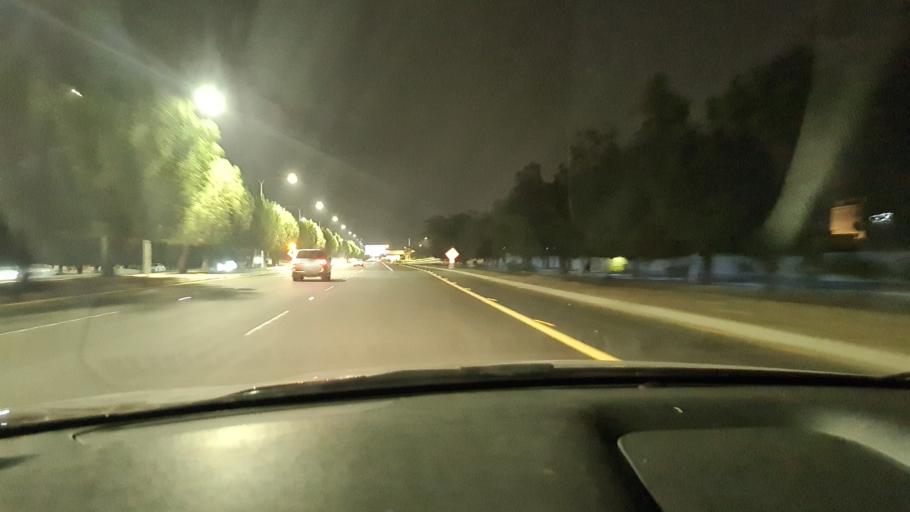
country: SA
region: Eastern Province
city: Al Jubayl
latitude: 27.1265
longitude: 49.5458
